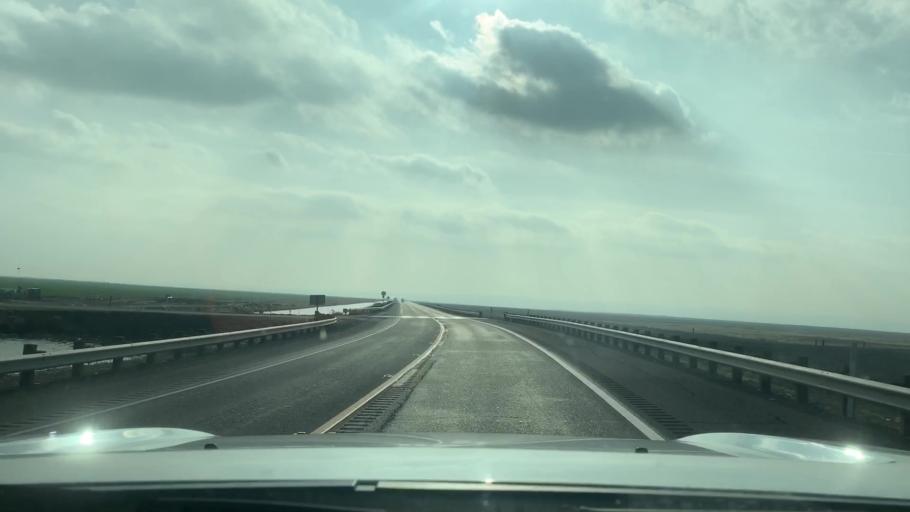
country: US
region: California
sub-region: Kings County
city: Stratford
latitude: 36.1224
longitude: -119.8928
